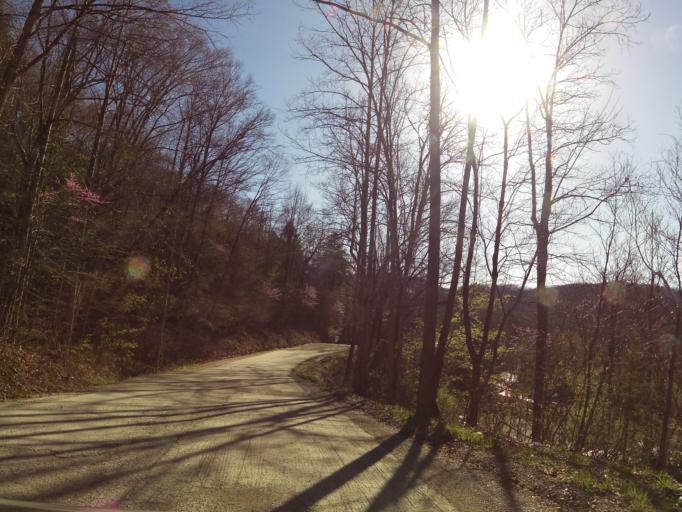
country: US
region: Tennessee
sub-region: Campbell County
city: Caryville
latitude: 36.3248
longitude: -84.3687
